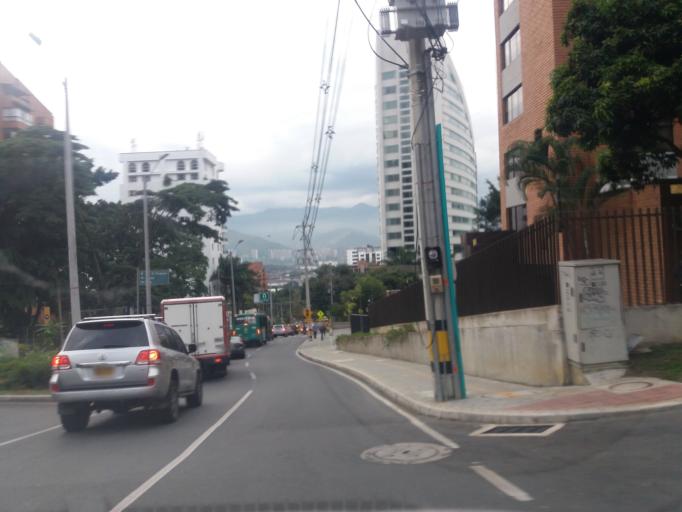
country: CO
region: Antioquia
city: Itagui
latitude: 6.2028
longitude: -75.5697
